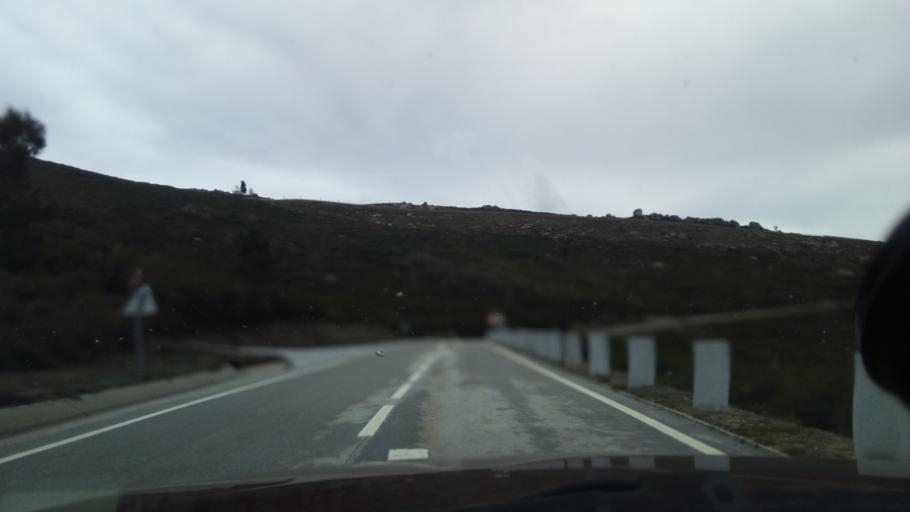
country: PT
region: Guarda
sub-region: Seia
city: Seia
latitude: 40.3488
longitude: -7.7013
